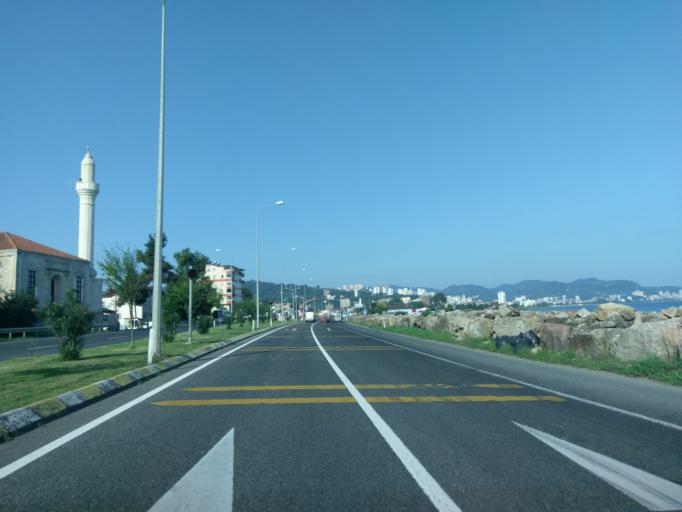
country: TR
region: Ordu
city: Fatsa
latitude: 41.0215
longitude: 37.5397
